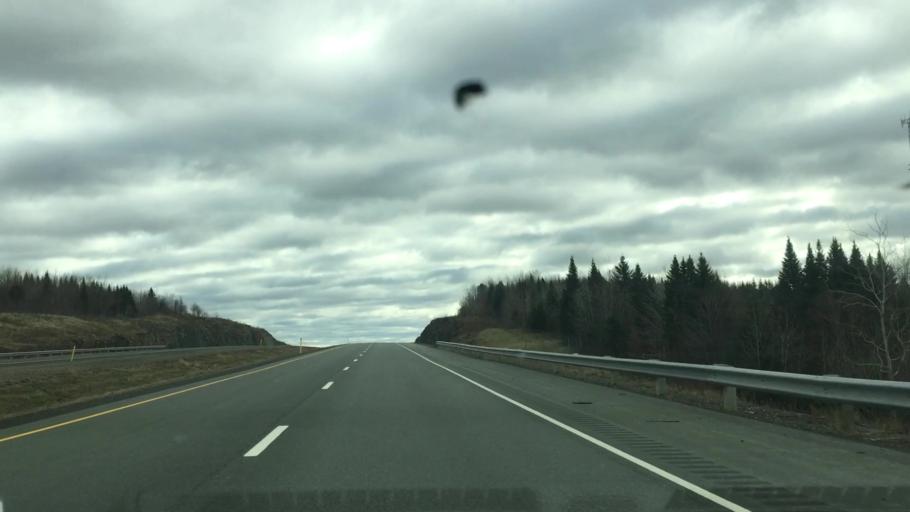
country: CA
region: New Brunswick
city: Florenceville-Bristol
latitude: 46.5515
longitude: -67.7357
